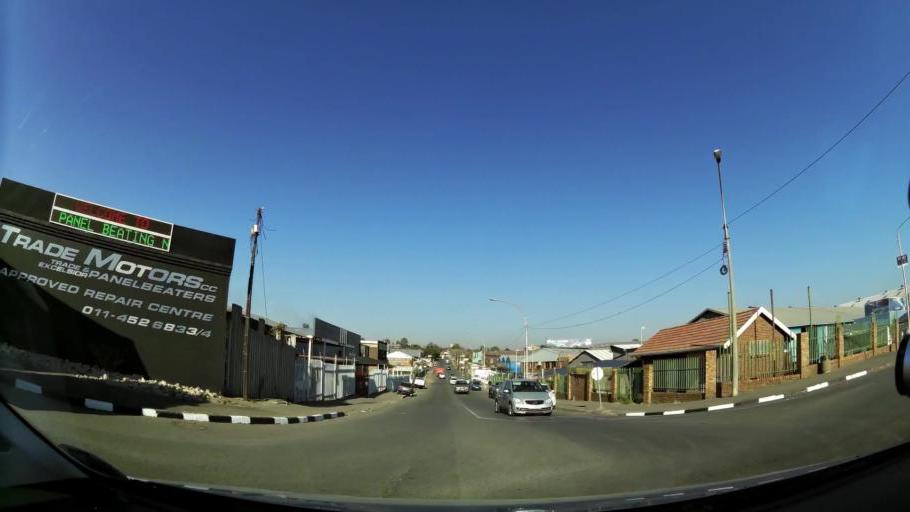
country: ZA
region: Gauteng
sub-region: City of Johannesburg Metropolitan Municipality
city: Modderfontein
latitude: -26.1309
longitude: 28.1592
